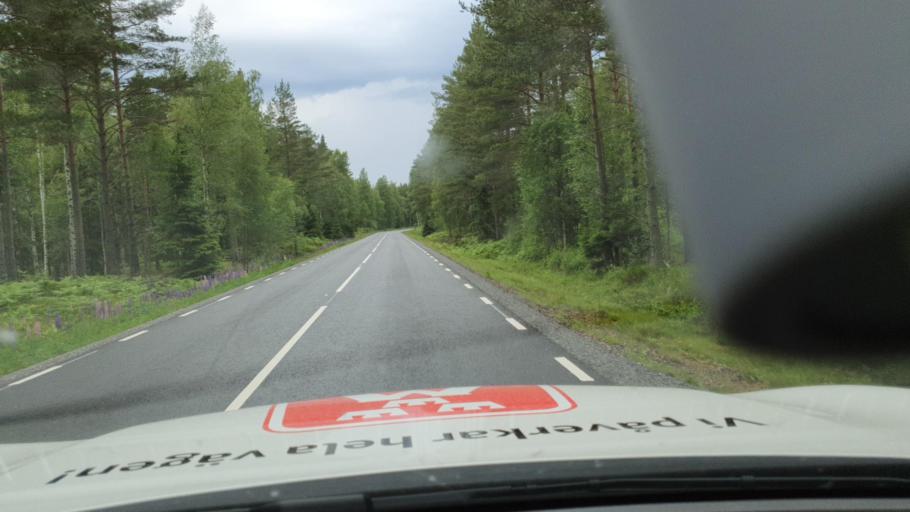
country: SE
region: OErebro
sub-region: Laxa Kommun
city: Laxa
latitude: 58.8803
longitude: 14.5025
